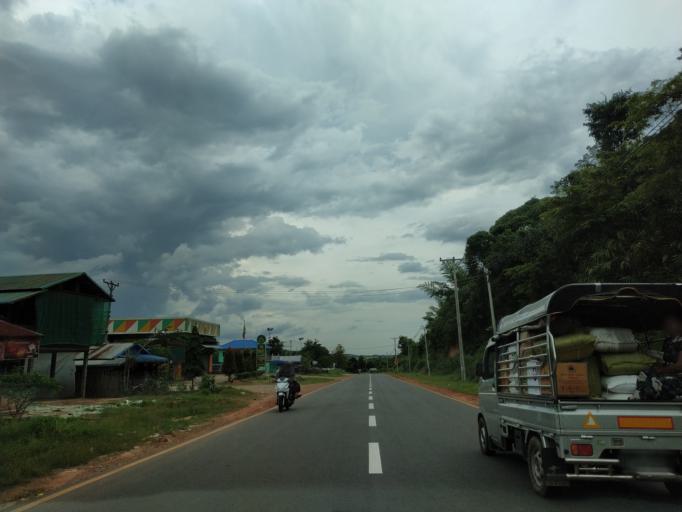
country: MM
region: Tanintharyi
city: Dawei
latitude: 14.0037
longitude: 98.2277
